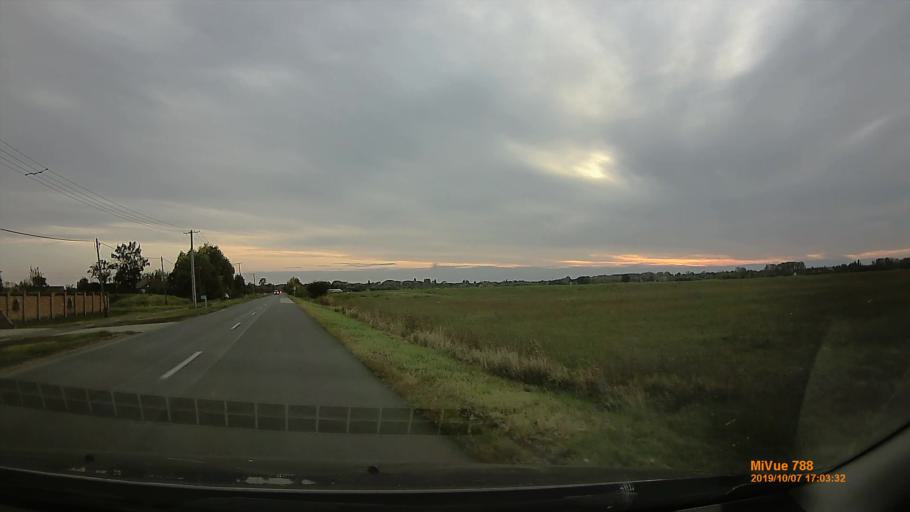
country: HU
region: Bekes
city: Szarvas
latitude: 46.8435
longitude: 20.5510
